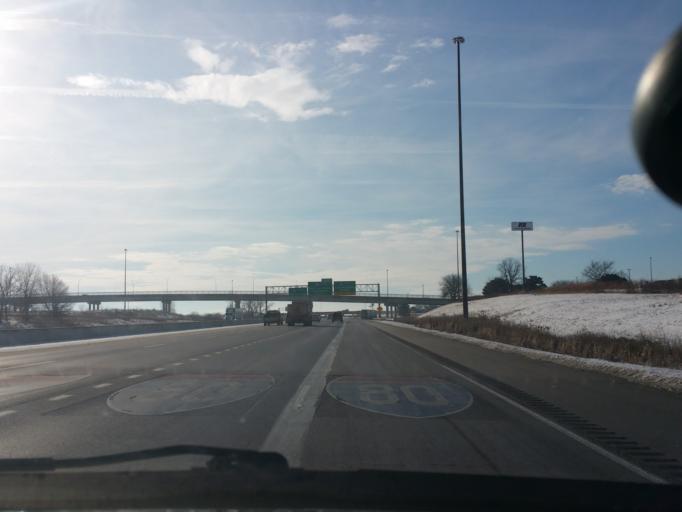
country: US
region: Iowa
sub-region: Polk County
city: Clive
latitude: 41.5991
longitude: -93.7772
